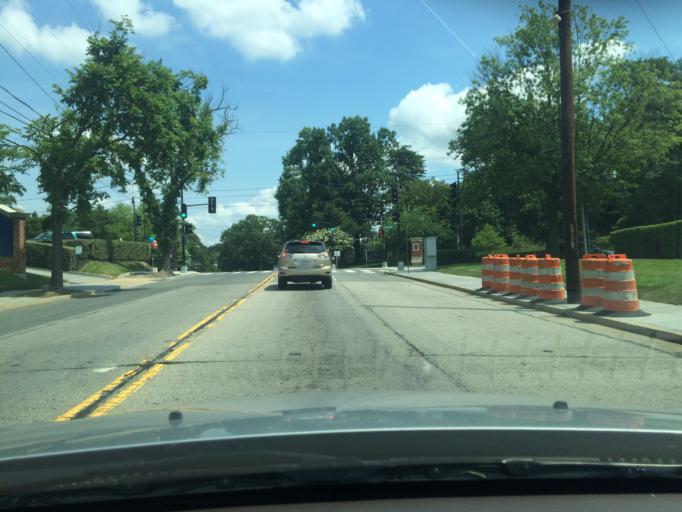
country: US
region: Maryland
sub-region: Prince George's County
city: Chillum
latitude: 38.9537
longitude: -76.9881
